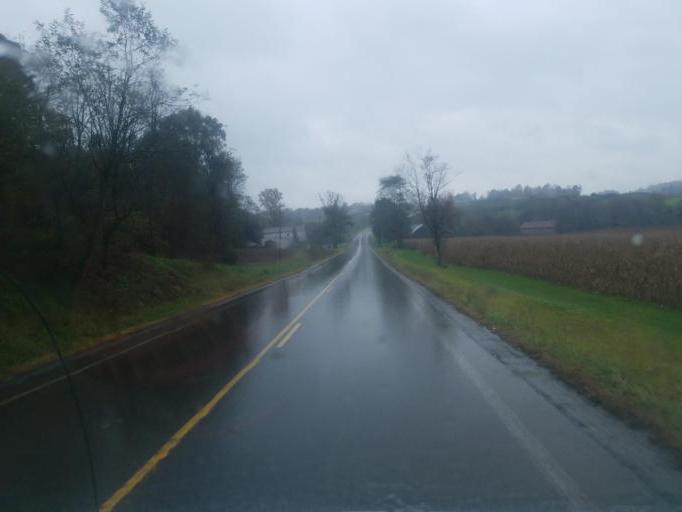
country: US
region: Ohio
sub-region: Licking County
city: Utica
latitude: 40.2466
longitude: -82.3199
